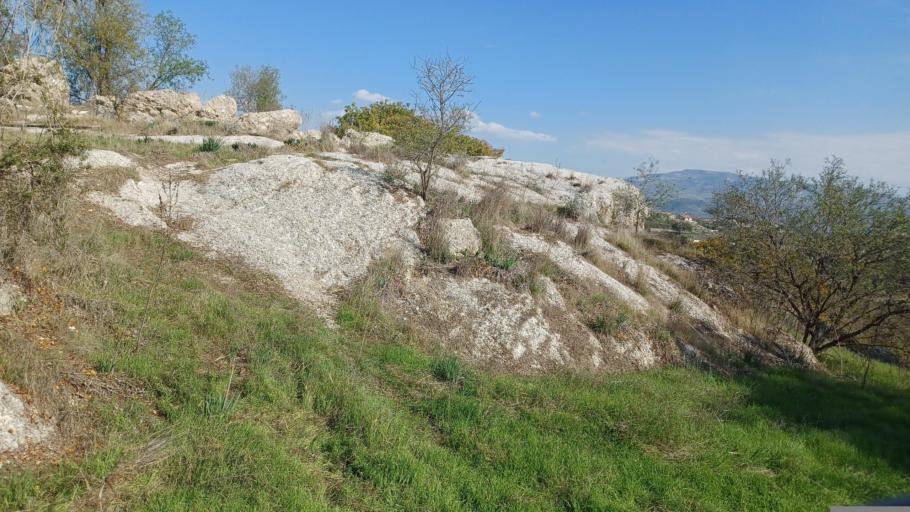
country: CY
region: Pafos
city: Mesogi
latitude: 34.8500
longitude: 32.5138
